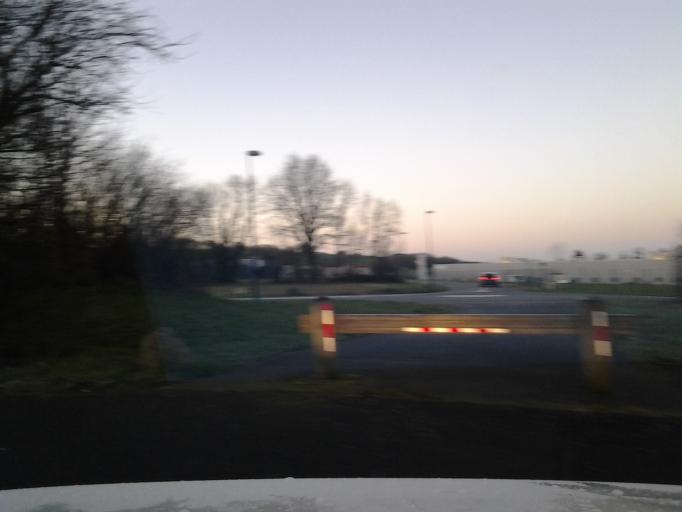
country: FR
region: Pays de la Loire
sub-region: Departement de la Vendee
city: Les Epesses
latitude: 46.8773
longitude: -0.9040
